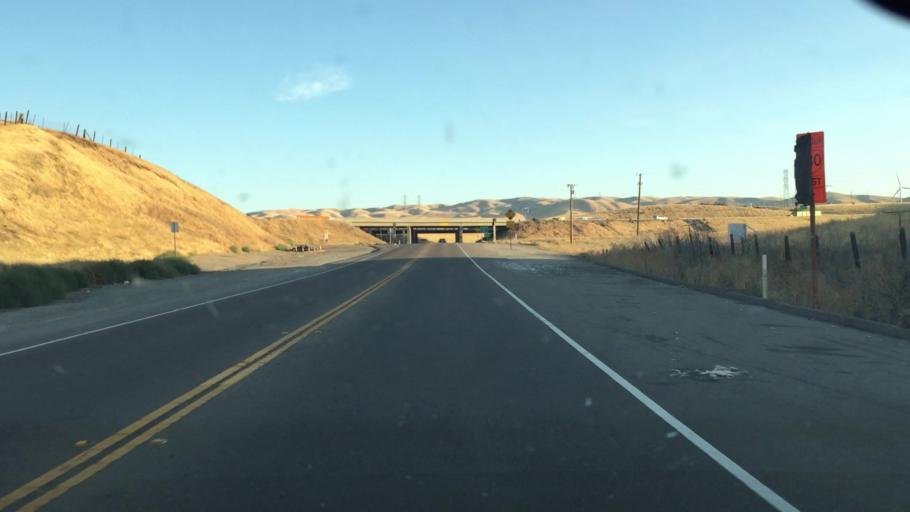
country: US
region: California
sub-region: San Joaquin County
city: Mountain House
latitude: 37.7426
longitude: -121.5852
